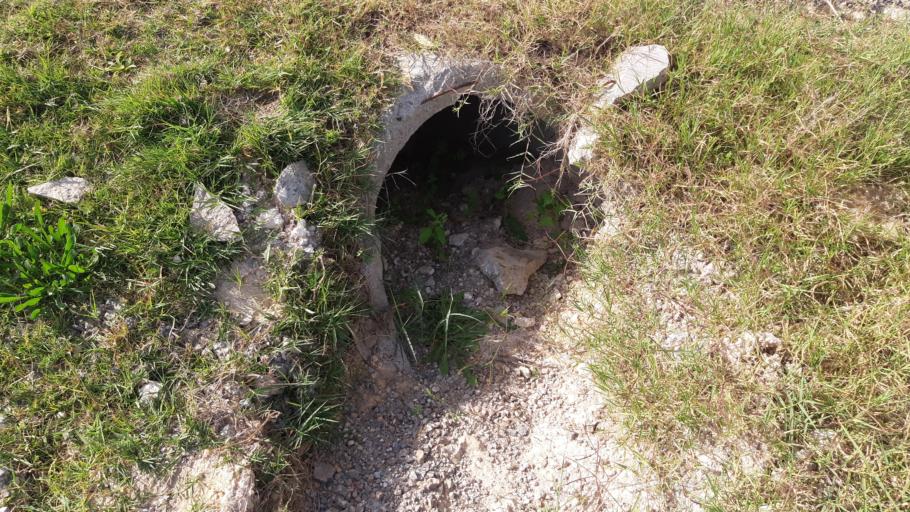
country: TN
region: Al Munastir
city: Sidi Bin Nur
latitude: 35.4516
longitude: 10.9061
